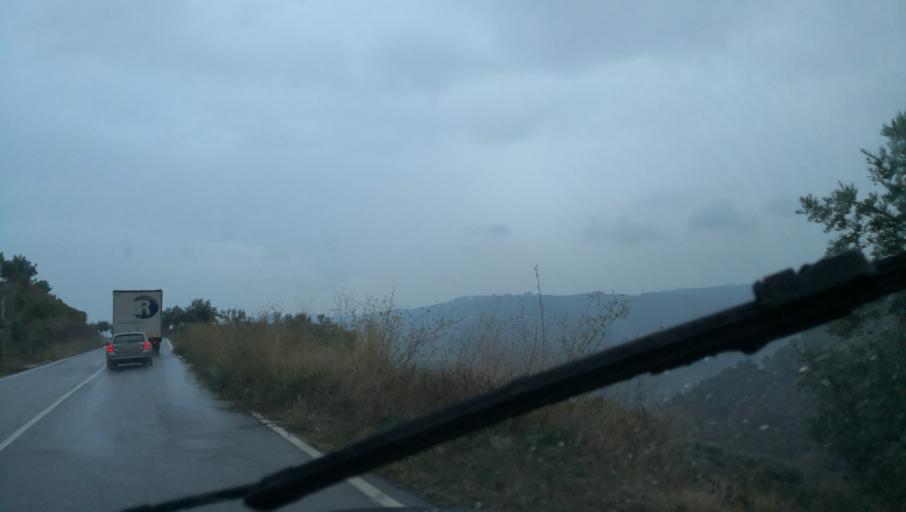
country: PT
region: Vila Real
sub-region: Santa Marta de Penaguiao
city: Santa Marta de Penaguiao
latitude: 41.2239
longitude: -7.7302
